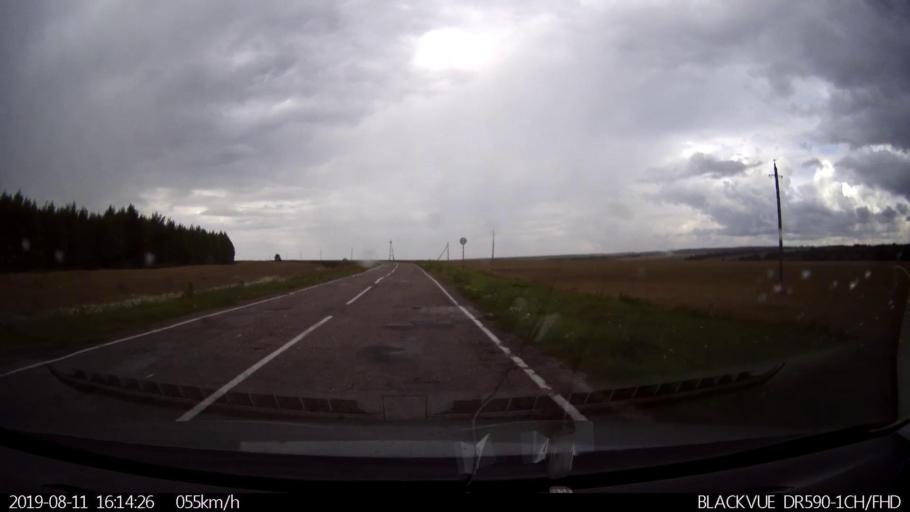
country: RU
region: Ulyanovsk
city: Ignatovka
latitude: 54.0280
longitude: 47.6341
